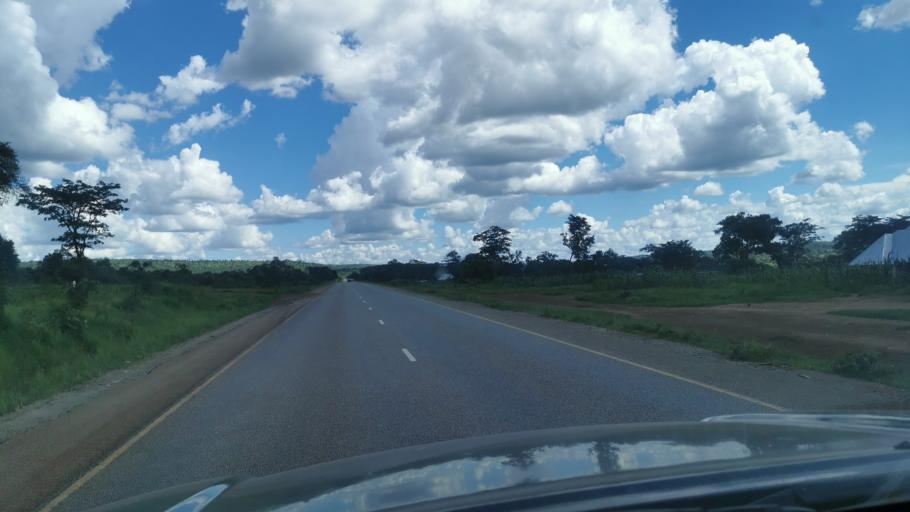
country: TZ
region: Geita
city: Uyovu
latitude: -3.0932
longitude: 31.2979
